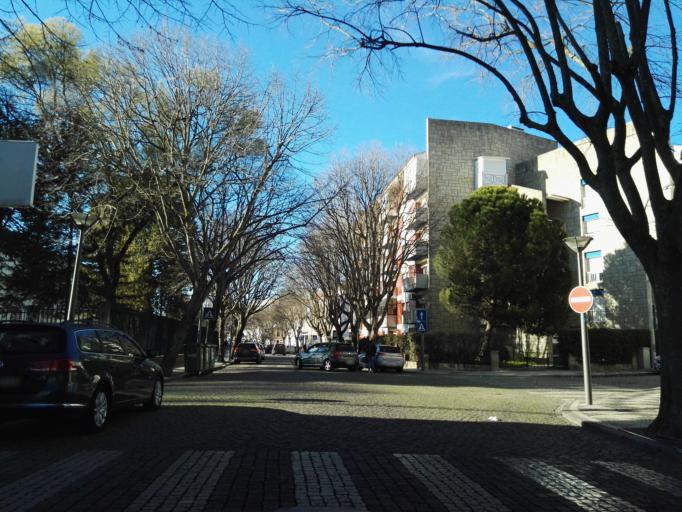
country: PT
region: Castelo Branco
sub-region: Castelo Branco
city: Castelo Branco
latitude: 39.8205
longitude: -7.4973
